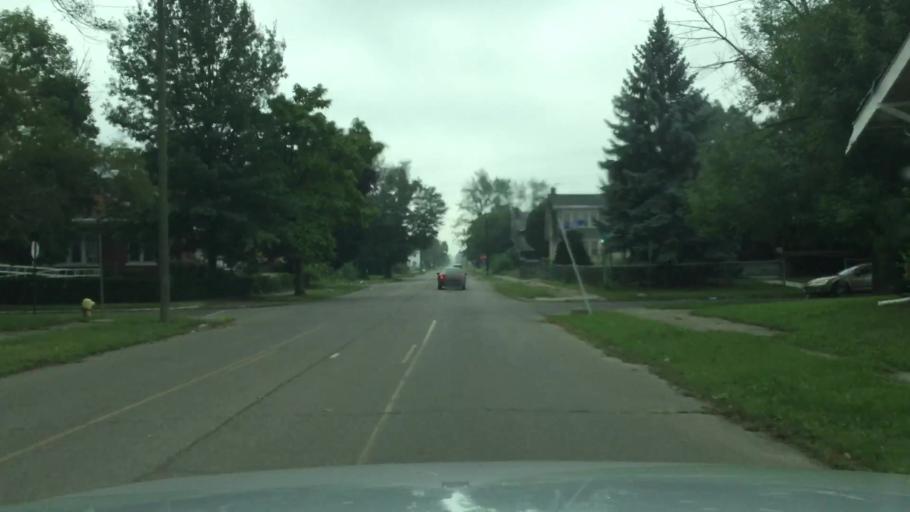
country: US
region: Michigan
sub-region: Wayne County
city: Highland Park
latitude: 42.4124
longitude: -83.1092
